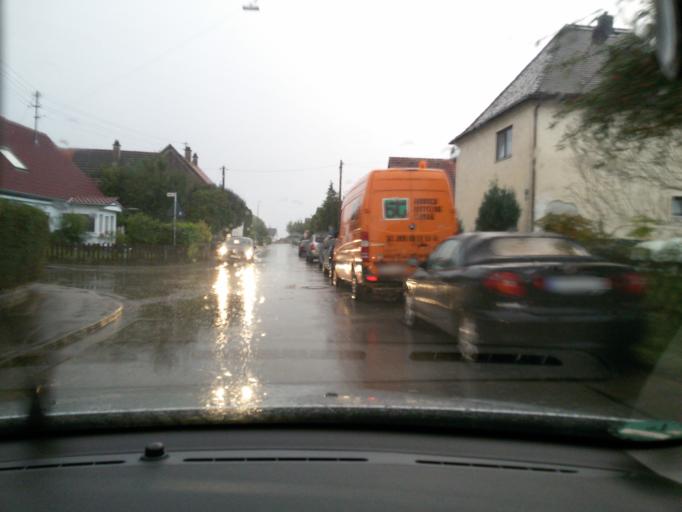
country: DE
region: Bavaria
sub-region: Swabia
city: Hiltenfingen
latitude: 48.1622
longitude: 10.7215
